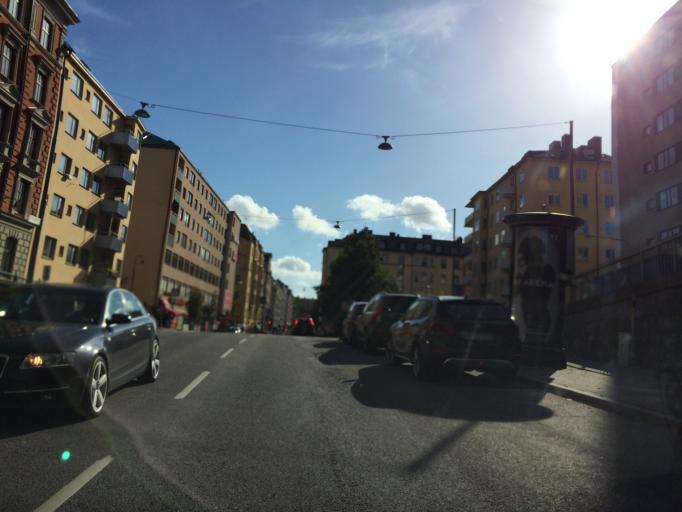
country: SE
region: Stockholm
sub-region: Stockholms Kommun
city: Stockholm
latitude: 59.3193
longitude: 18.0564
